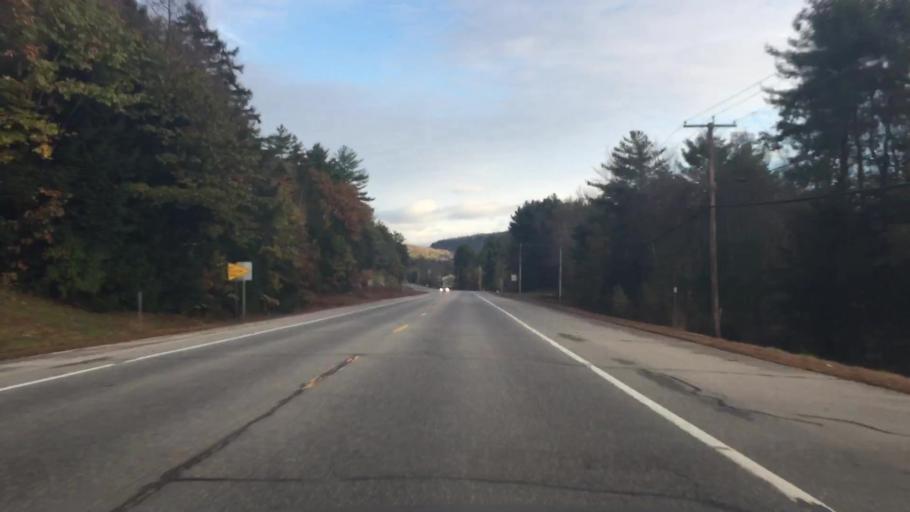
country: US
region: New Hampshire
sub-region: Cheshire County
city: Keene
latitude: 42.9967
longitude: -72.2588
